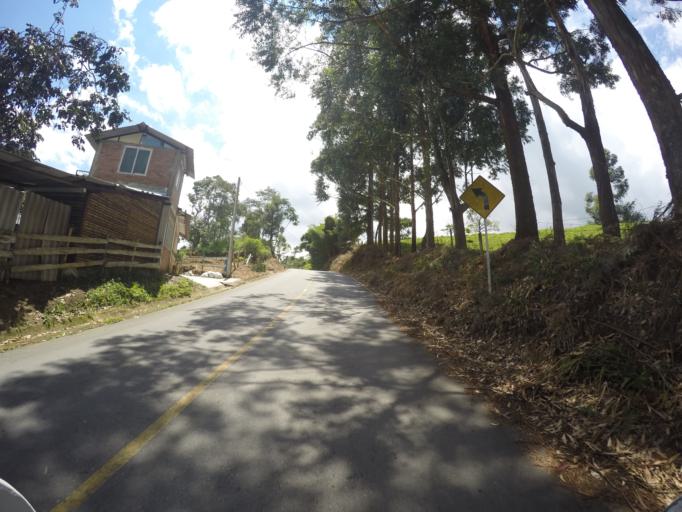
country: CO
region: Quindio
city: Filandia
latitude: 4.6511
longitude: -75.6785
